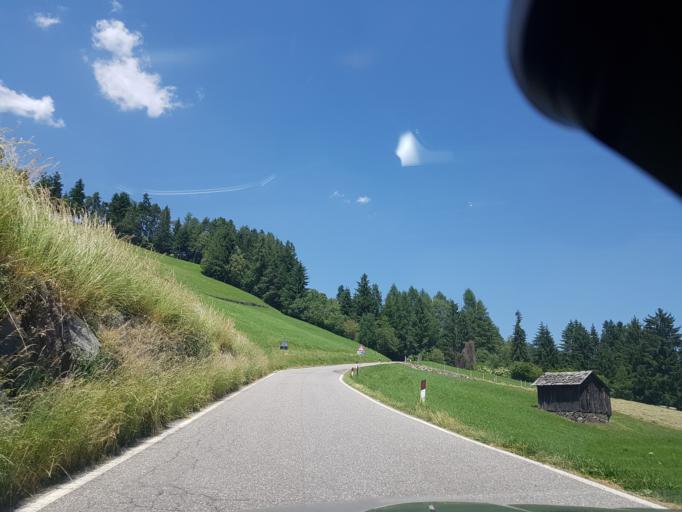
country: IT
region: Trentino-Alto Adige
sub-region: Bolzano
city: Villandro - Villanders
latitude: 46.6421
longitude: 11.5321
